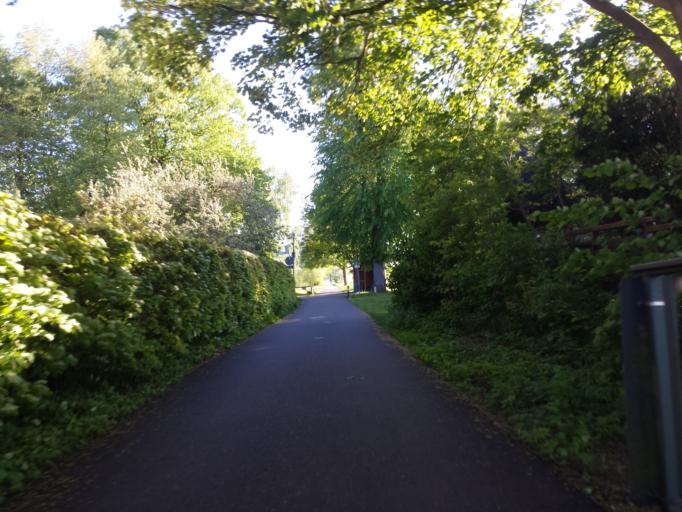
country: DE
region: Lower Saxony
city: Lilienthal
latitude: 53.1216
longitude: 8.8840
